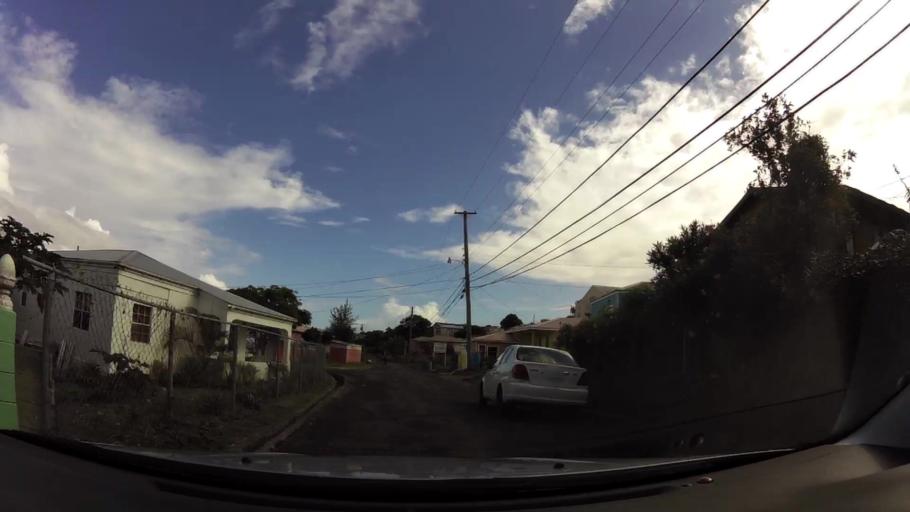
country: AG
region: Saint George
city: Piggotts
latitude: 17.1145
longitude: -61.8222
